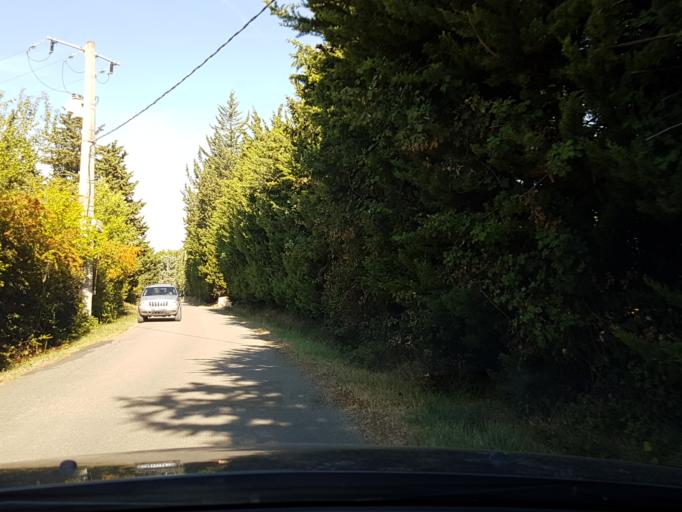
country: FR
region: Provence-Alpes-Cote d'Azur
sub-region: Departement des Bouches-du-Rhone
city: Eygalieres
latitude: 43.7659
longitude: 4.9648
